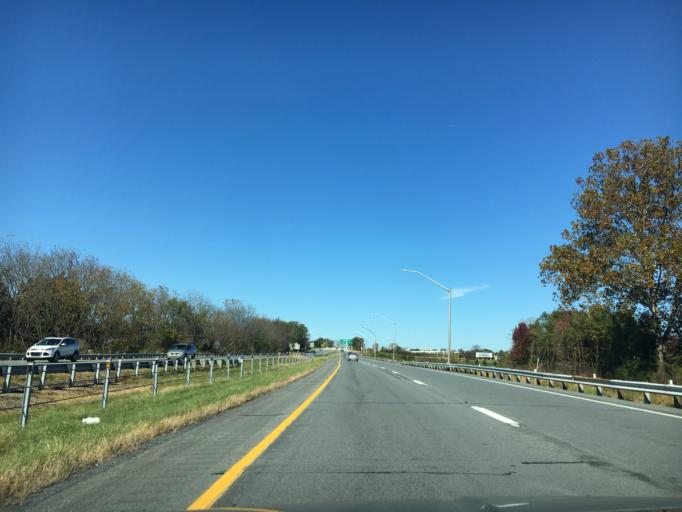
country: US
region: Pennsylvania
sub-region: Northampton County
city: Bethlehem
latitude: 40.6434
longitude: -75.4113
